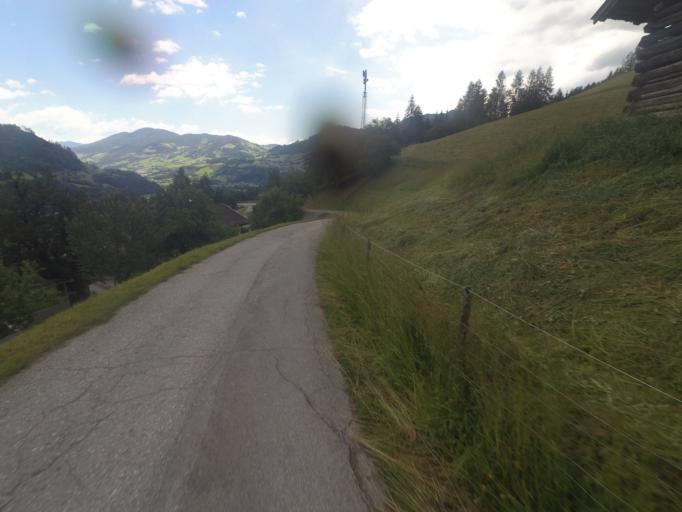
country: AT
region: Salzburg
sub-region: Politischer Bezirk Sankt Johann im Pongau
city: Schwarzach im Pongau
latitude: 47.3137
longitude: 13.1587
